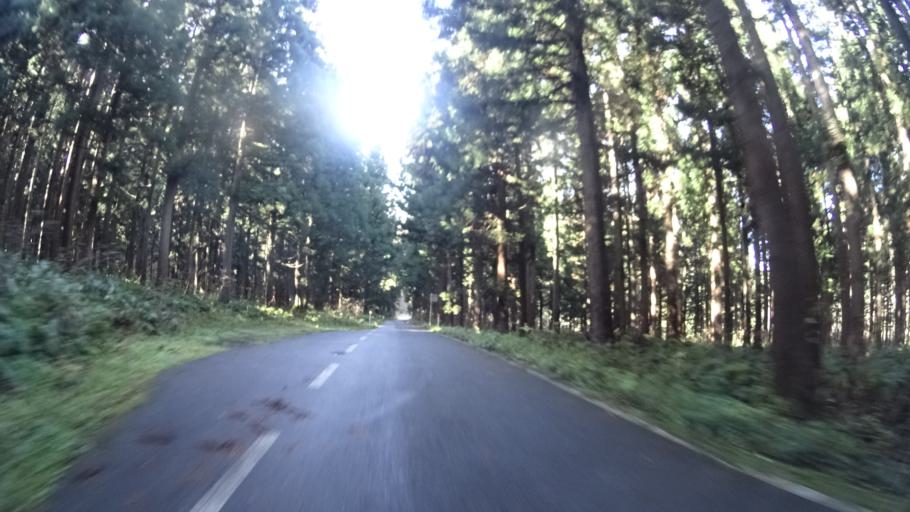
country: JP
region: Niigata
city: Muikamachi
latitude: 37.1796
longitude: 139.0839
